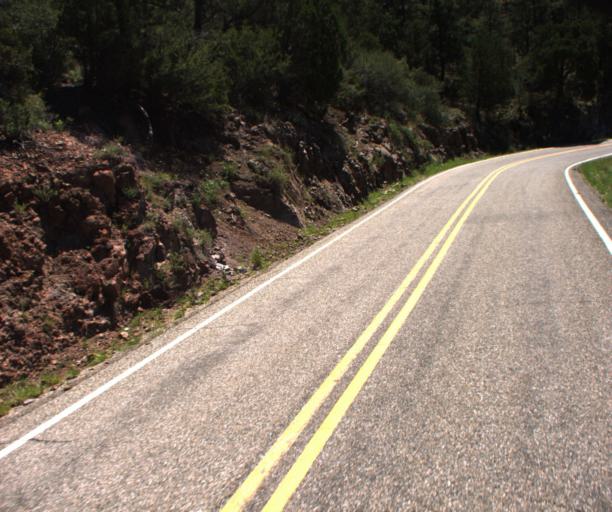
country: US
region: Arizona
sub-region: Greenlee County
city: Morenci
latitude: 33.2414
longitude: -109.3769
